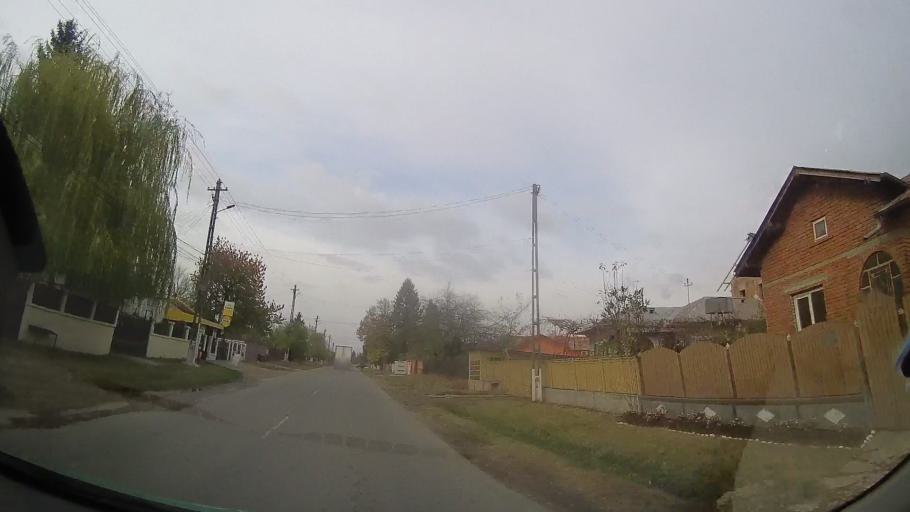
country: RO
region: Prahova
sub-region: Comuna Gorgota
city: Potigrafu
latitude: 44.7746
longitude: 26.1064
